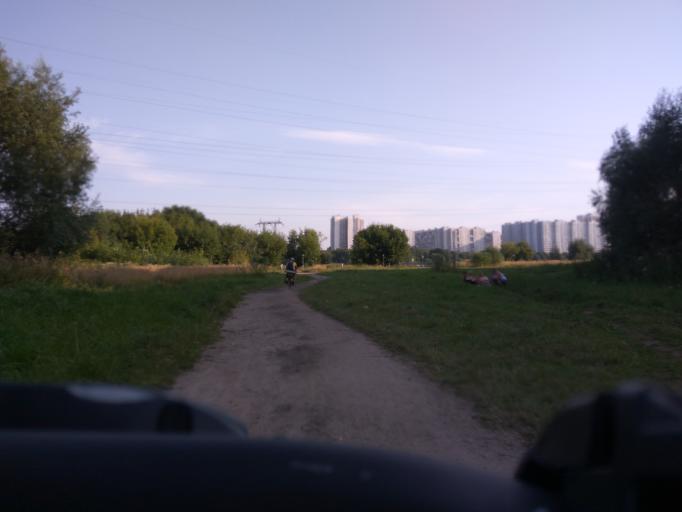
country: RU
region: Moscow
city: Brateyevo
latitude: 55.6501
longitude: 37.7722
